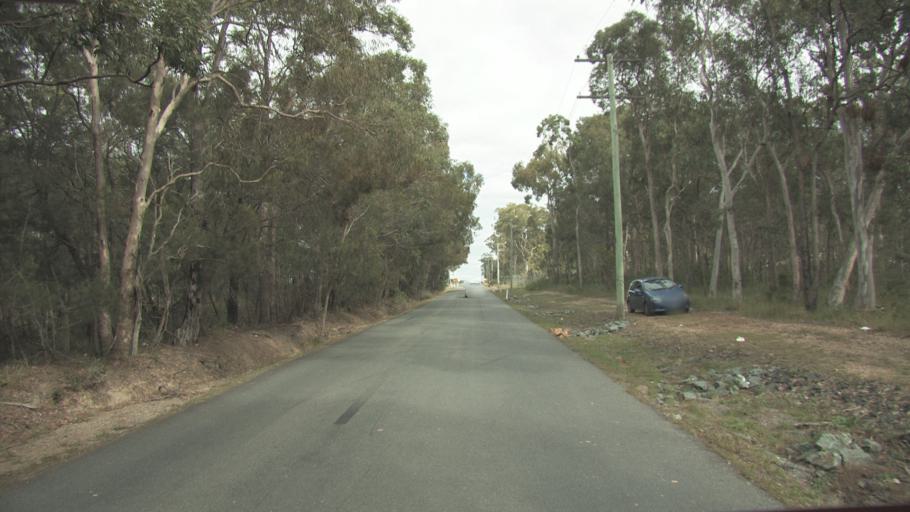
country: AU
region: Queensland
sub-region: Logan
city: Woodridge
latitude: -27.6533
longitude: 153.0853
